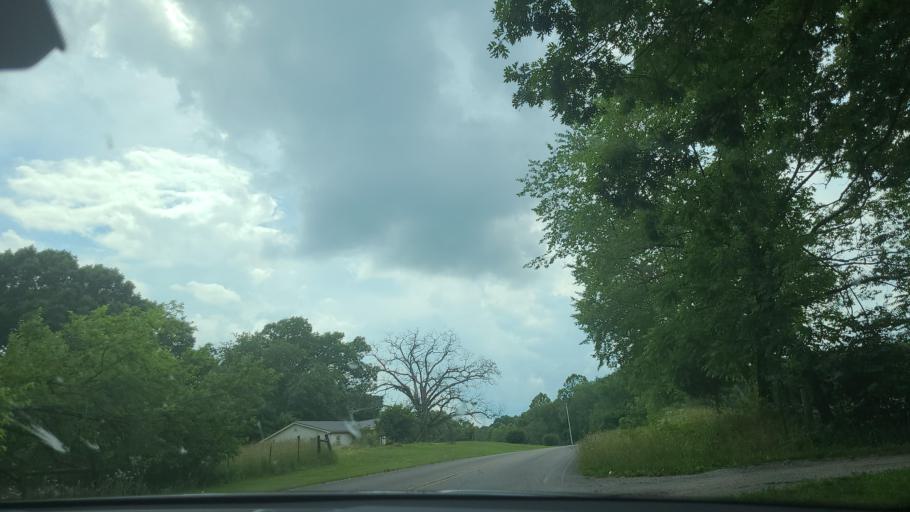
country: US
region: Tennessee
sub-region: Cumberland County
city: Lake Tansi
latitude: 35.7857
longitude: -85.0544
